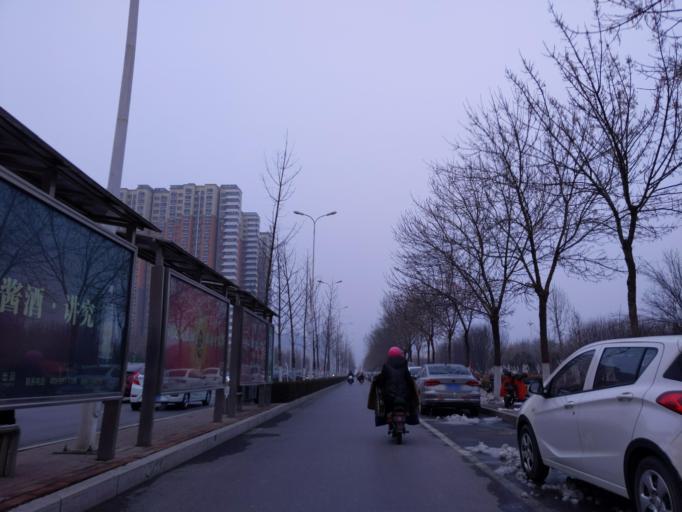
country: CN
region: Henan Sheng
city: Puyang
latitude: 35.7775
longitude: 115.0264
